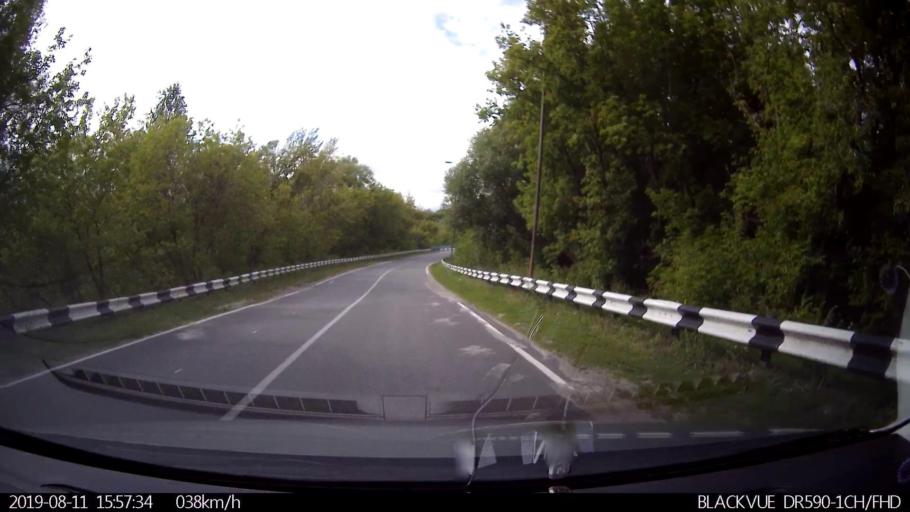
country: RU
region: Ulyanovsk
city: Ignatovka
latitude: 53.9514
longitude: 47.6522
